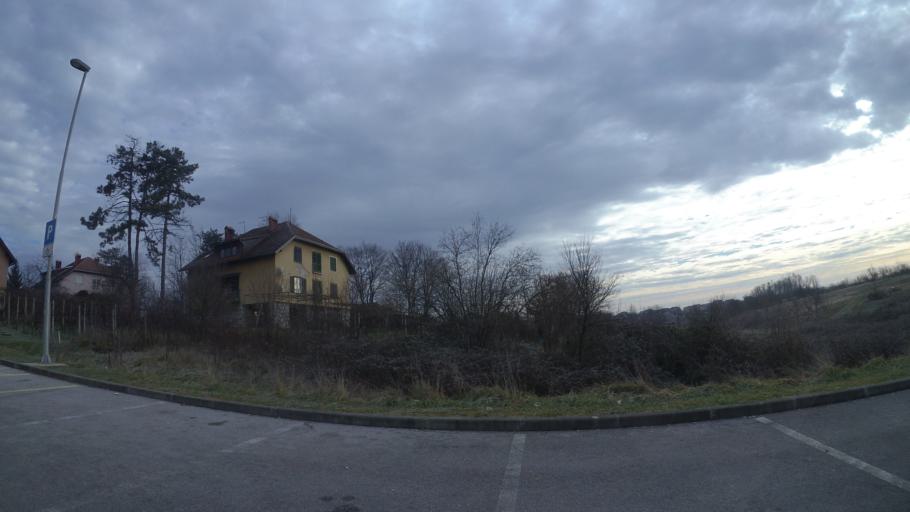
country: HR
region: Karlovacka
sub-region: Grad Karlovac
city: Karlovac
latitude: 45.4719
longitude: 15.5461
